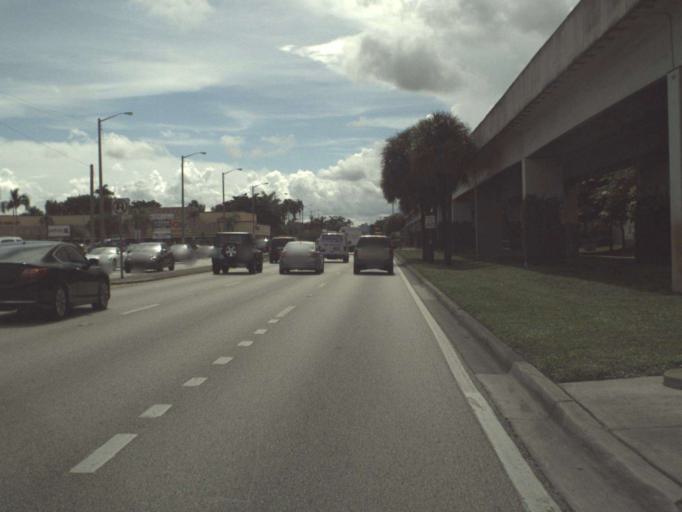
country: US
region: Florida
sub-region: Miami-Dade County
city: South Miami
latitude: 25.7014
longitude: -80.2934
